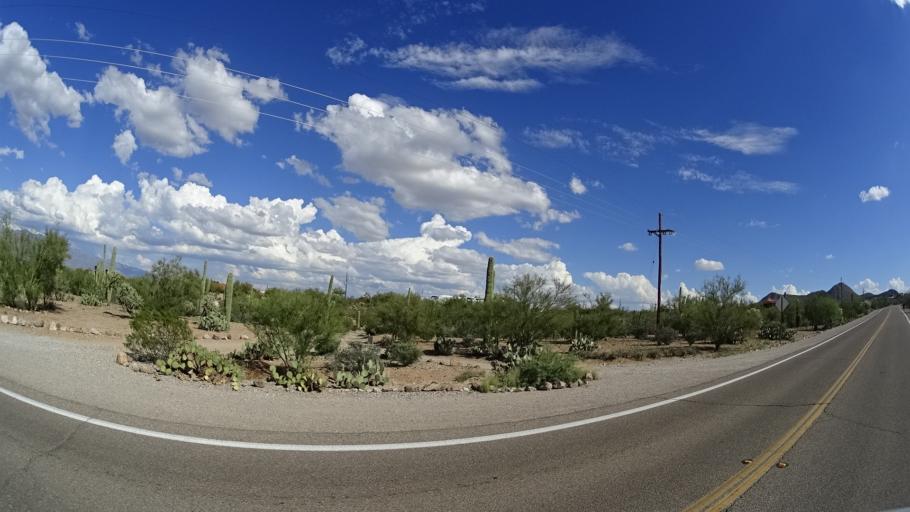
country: US
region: Arizona
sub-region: Pima County
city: Flowing Wells
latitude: 32.2562
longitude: -111.0613
